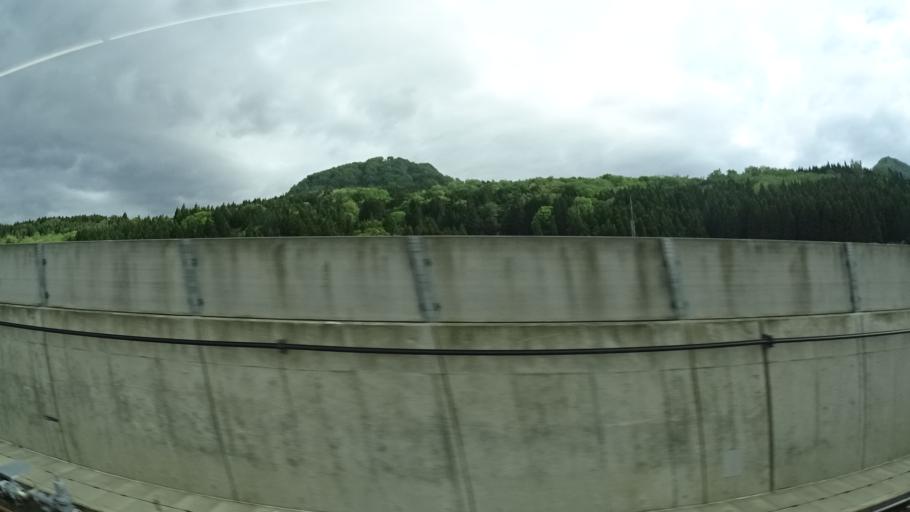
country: JP
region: Niigata
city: Itoigawa
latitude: 37.0862
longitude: 138.0070
